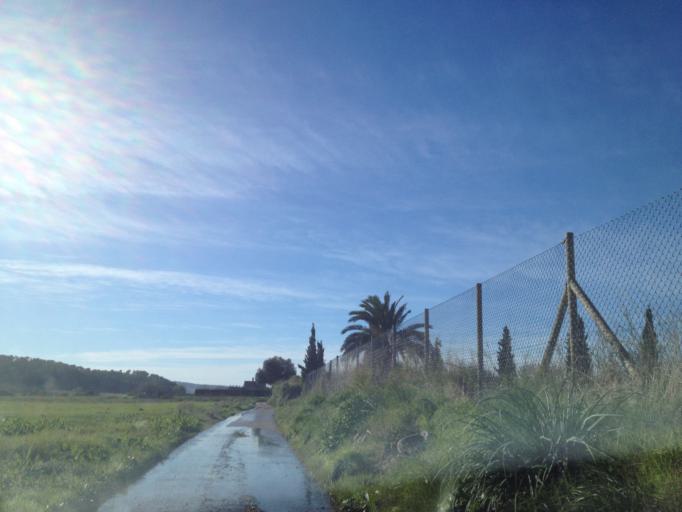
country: ES
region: Balearic Islands
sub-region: Illes Balears
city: Sineu
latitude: 39.6492
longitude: 3.0364
